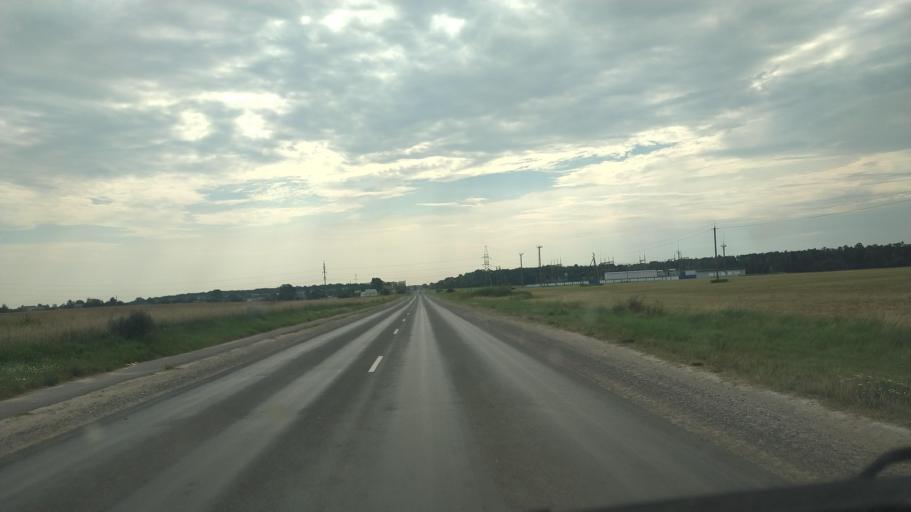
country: BY
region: Brest
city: Byaroza
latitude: 52.5494
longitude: 24.9443
